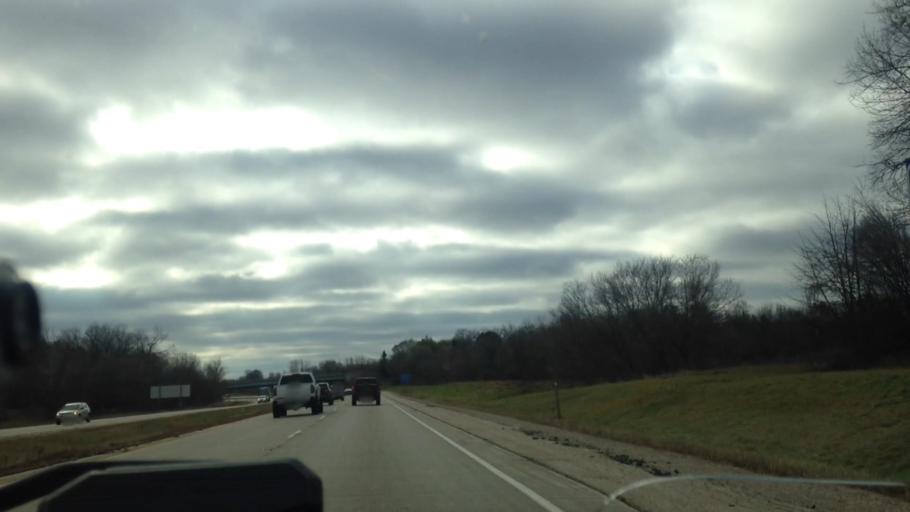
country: US
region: Wisconsin
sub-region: Washington County
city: West Bend
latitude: 43.4167
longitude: -88.2070
